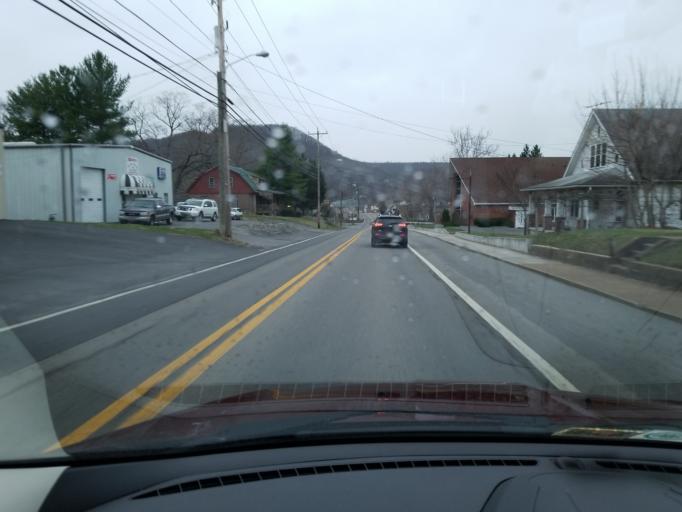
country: US
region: Virginia
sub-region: Giles County
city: Narrows
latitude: 37.3962
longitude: -80.7952
